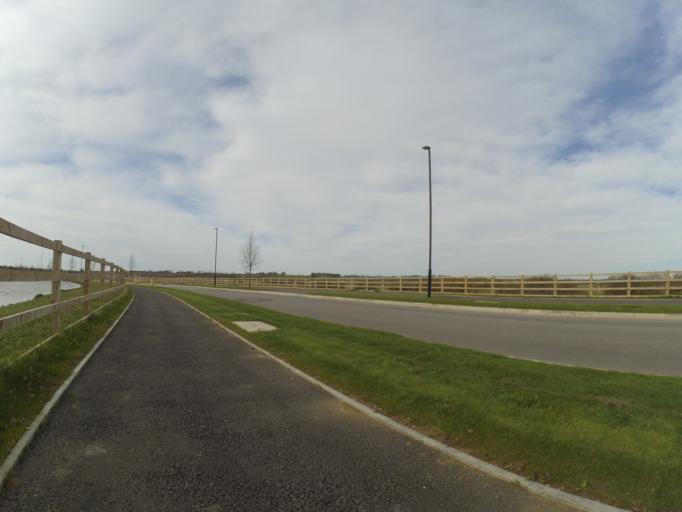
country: GB
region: England
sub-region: Warwickshire
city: Rugby
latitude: 52.3651
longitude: -1.1970
